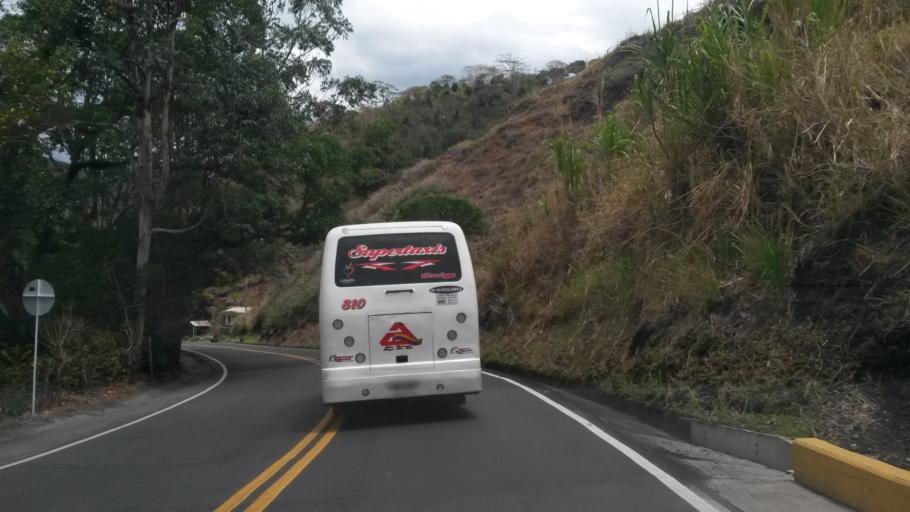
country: CO
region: Cauca
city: Rosas
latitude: 2.2812
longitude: -76.7153
